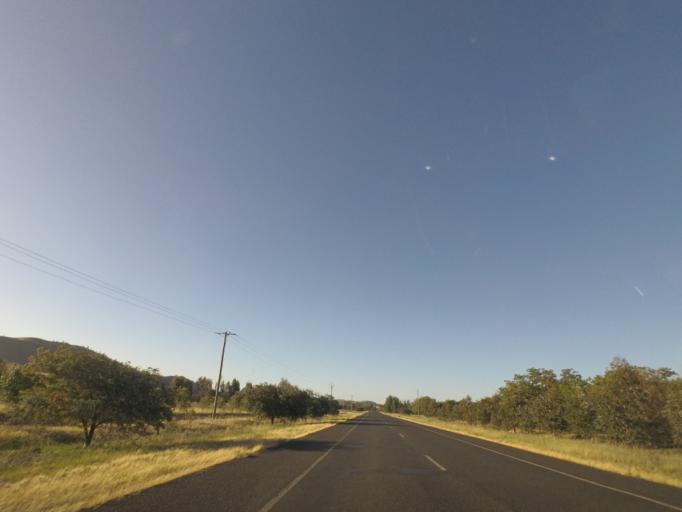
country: AU
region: New South Wales
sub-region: Gundagai
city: Gundagai
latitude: -34.9408
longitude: 148.1681
